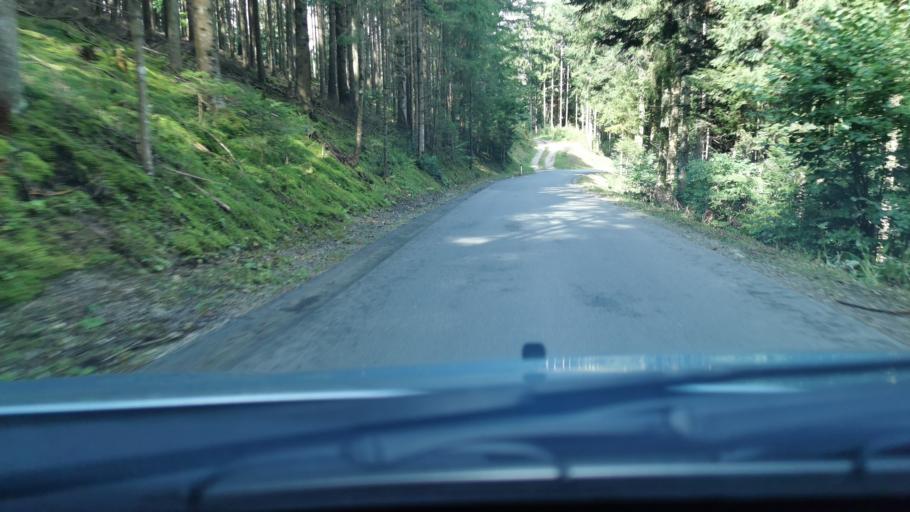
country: AT
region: Styria
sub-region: Politischer Bezirk Weiz
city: Birkfeld
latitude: 47.3363
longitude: 15.7054
